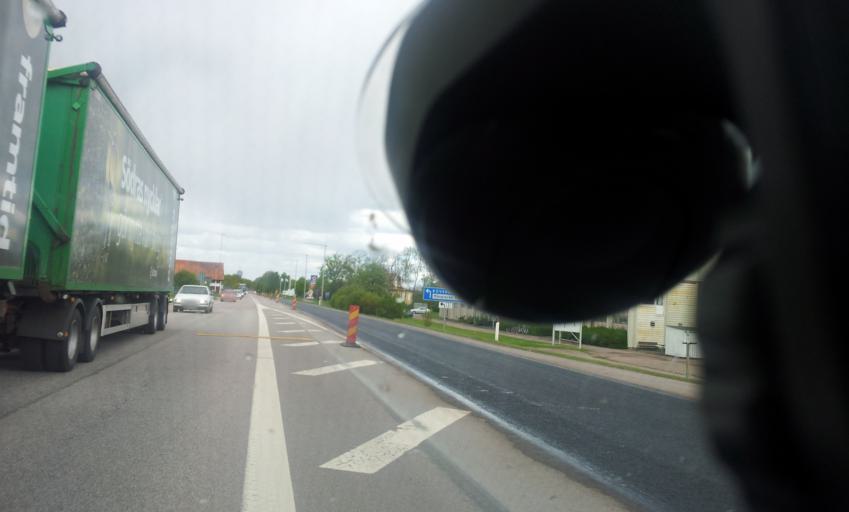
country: SE
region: Kalmar
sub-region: Monsteras Kommun
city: Moensteras
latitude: 57.0327
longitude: 16.4331
